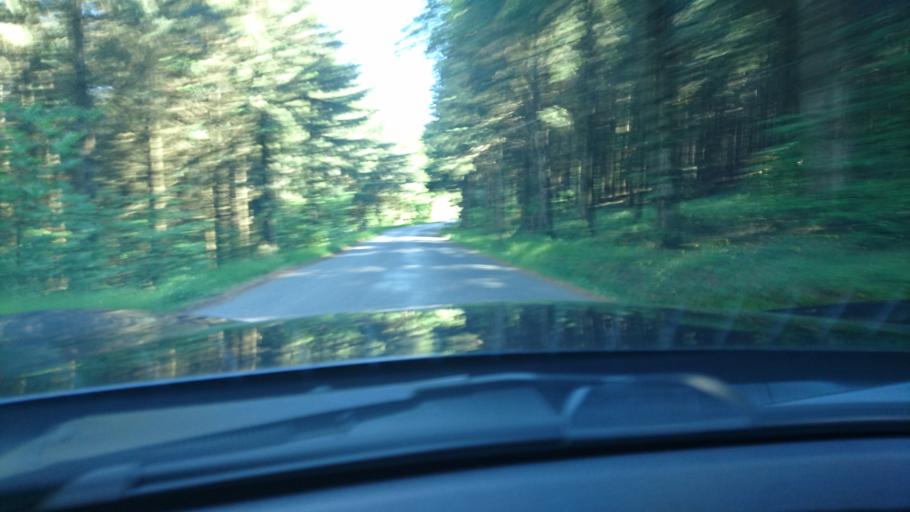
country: FR
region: Rhone-Alpes
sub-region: Departement de la Loire
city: Violay
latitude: 45.8243
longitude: 4.3853
